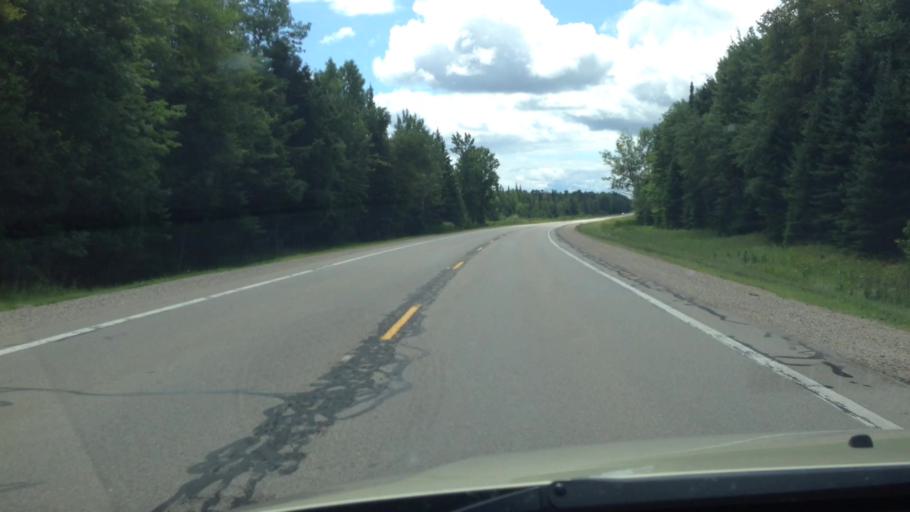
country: US
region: Michigan
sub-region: Menominee County
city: Menominee
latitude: 45.3582
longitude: -87.4000
